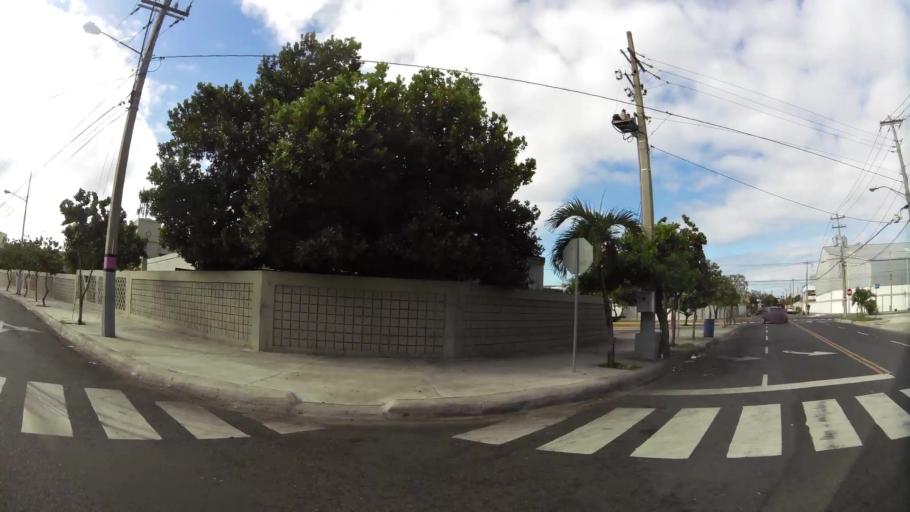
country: DO
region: Nacional
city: Bella Vista
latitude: 18.4475
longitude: -69.9284
